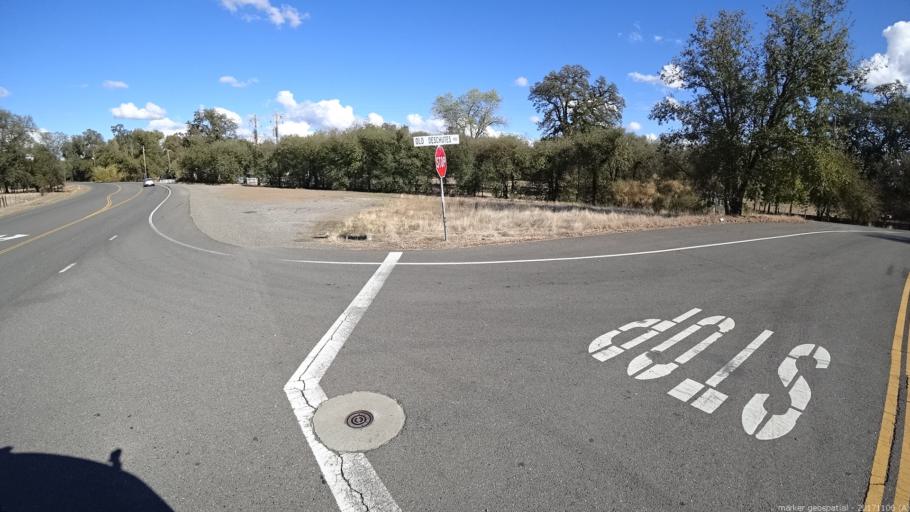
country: US
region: California
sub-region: Shasta County
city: Palo Cedro
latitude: 40.5958
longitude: -122.2348
